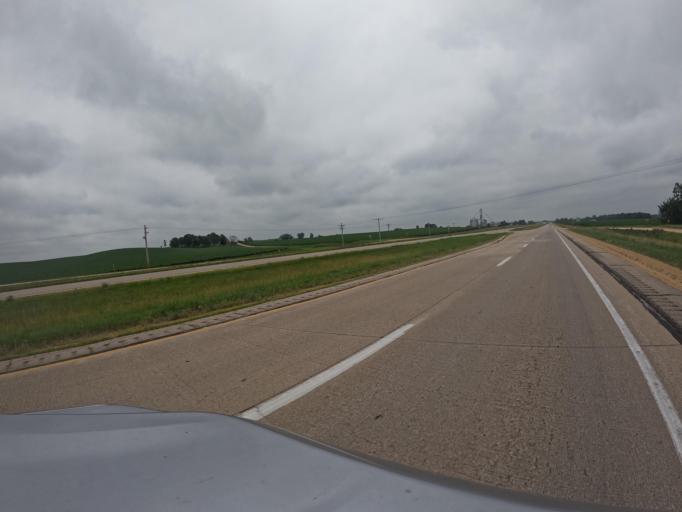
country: US
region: Iowa
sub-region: Clinton County
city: De Witt
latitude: 41.8914
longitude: -90.5877
